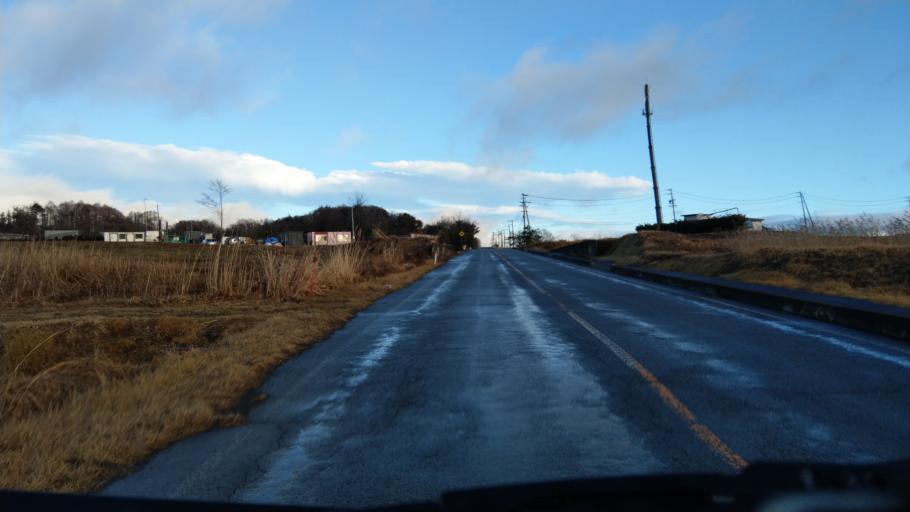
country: JP
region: Nagano
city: Komoro
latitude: 36.3040
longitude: 138.4030
